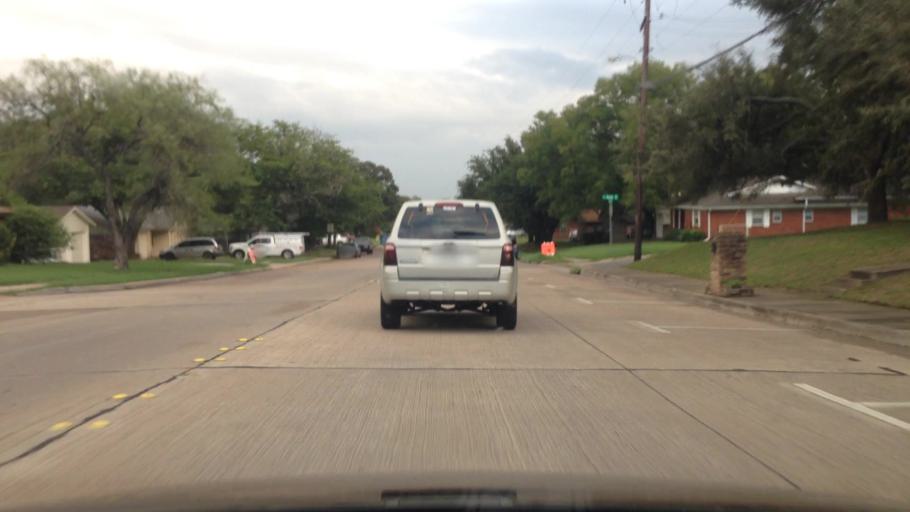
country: US
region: Texas
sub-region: Johnson County
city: Burleson
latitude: 32.5525
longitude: -97.3359
